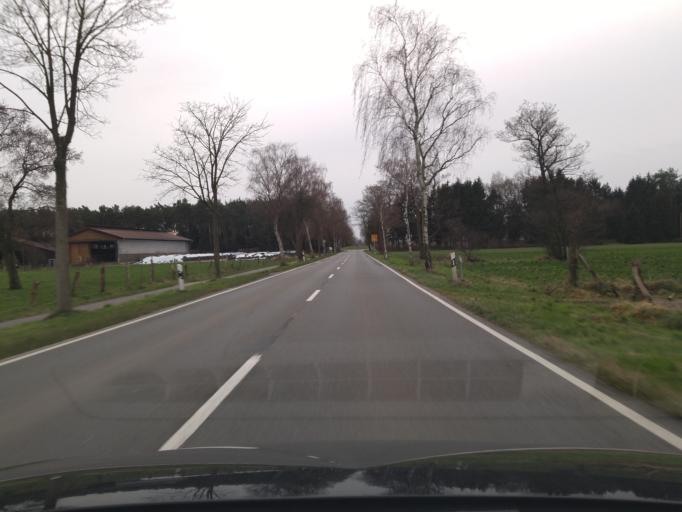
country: DE
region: Lower Saxony
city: Winsen (Aller)
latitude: 52.6960
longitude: 9.9133
